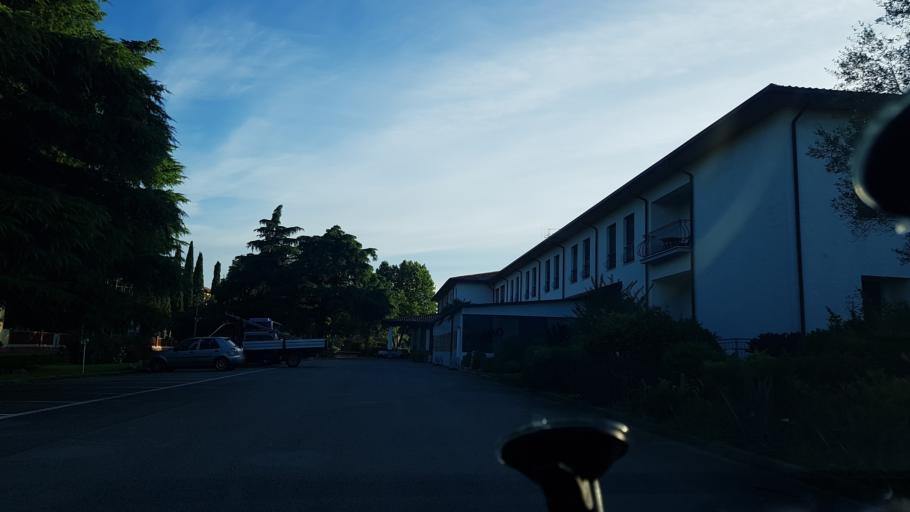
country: IT
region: Friuli Venezia Giulia
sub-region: Provincia di Gorizia
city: Gorizia
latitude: 45.9282
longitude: 13.6134
